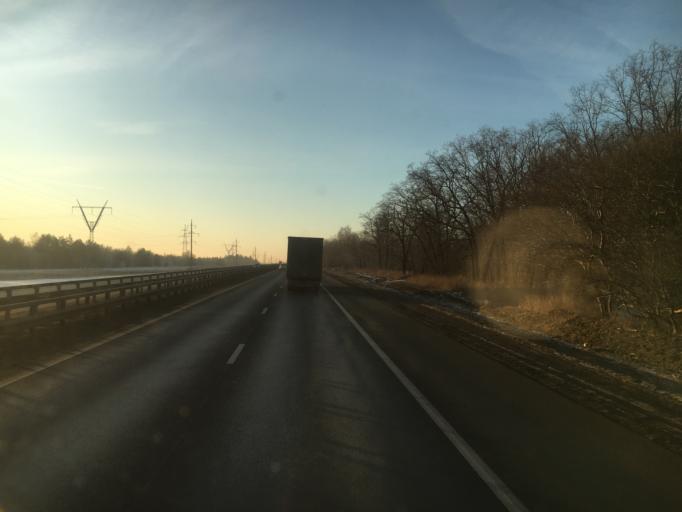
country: RU
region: Samara
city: Pribrezhnyy
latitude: 53.5185
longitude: 49.8086
